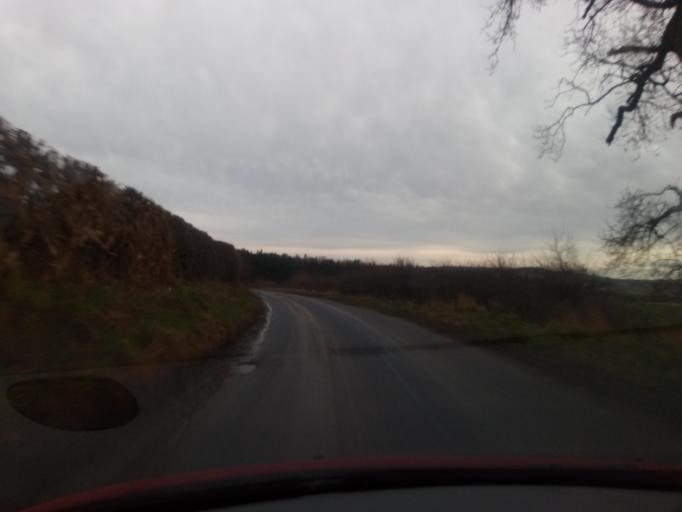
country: GB
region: England
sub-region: Northumberland
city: Whittingham
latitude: 55.4816
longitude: -1.8858
